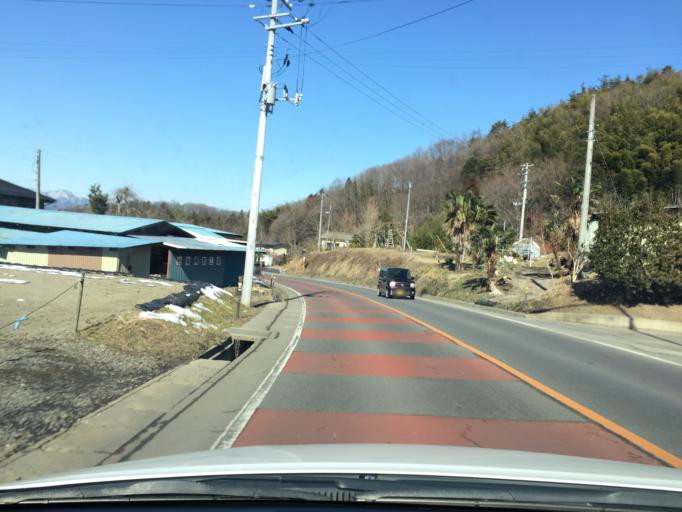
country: JP
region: Fukushima
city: Fukushima-shi
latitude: 37.7643
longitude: 140.5191
